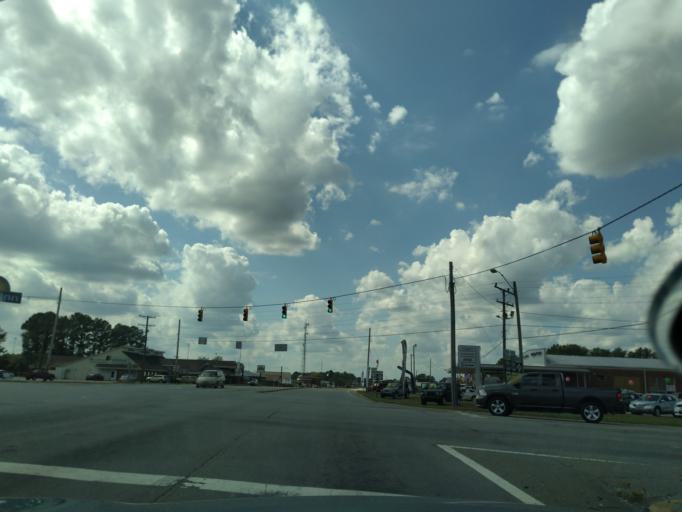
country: US
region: North Carolina
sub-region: Martin County
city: Williamston
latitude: 35.8417
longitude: -77.0632
